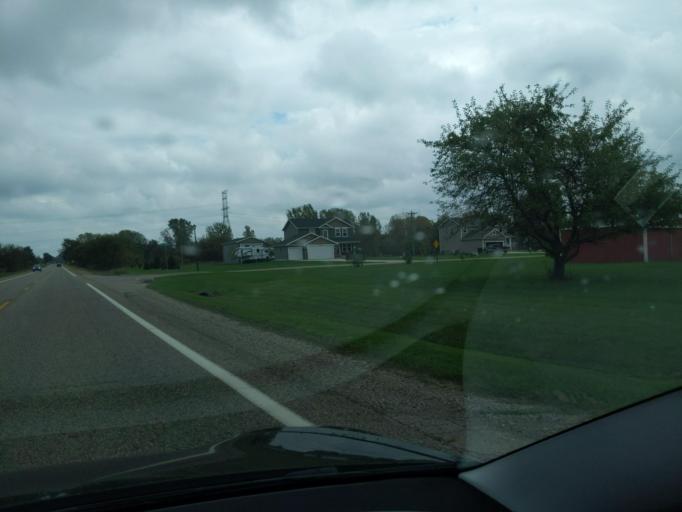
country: US
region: Michigan
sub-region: Eaton County
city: Charlotte
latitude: 42.5531
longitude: -84.7771
